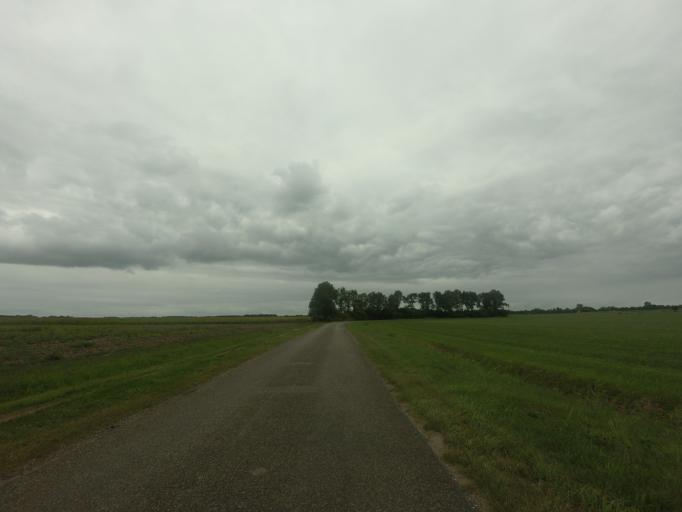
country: NL
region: Drenthe
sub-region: Gemeente Westerveld
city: Dwingeloo
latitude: 52.9647
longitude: 6.3143
